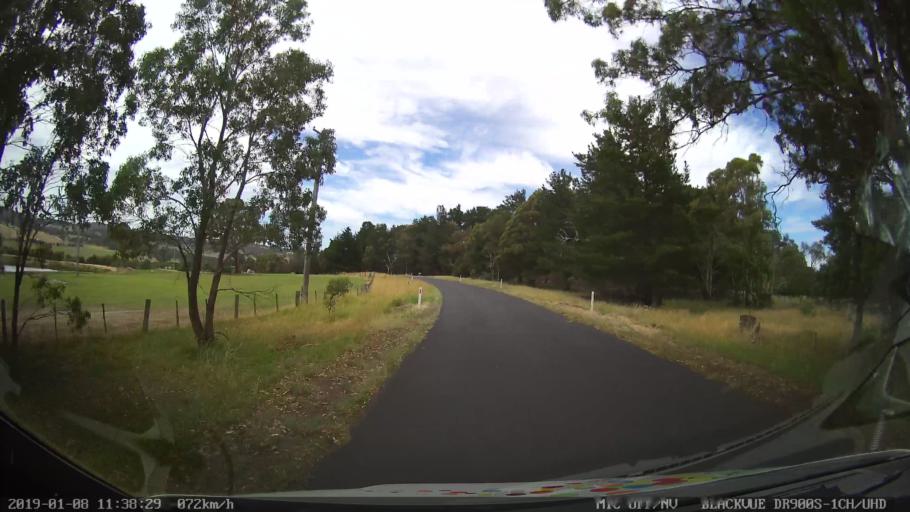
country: AU
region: New South Wales
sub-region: Armidale Dumaresq
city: Armidale
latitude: -30.3613
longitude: 151.5549
